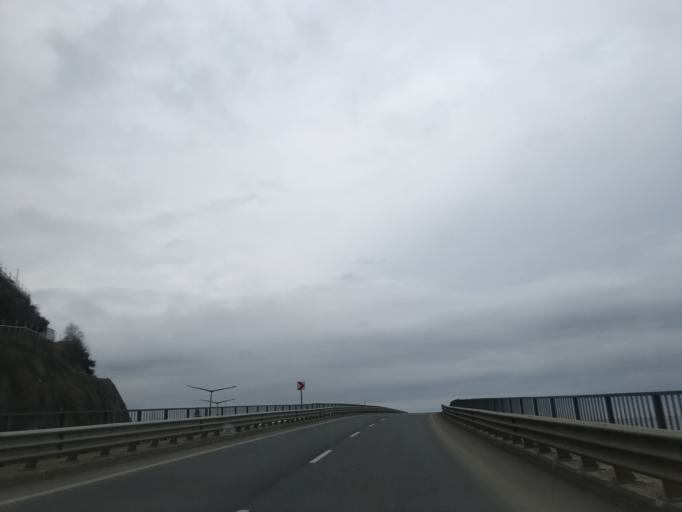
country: TR
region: Trabzon
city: Akcaabat
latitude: 41.0011
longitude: 39.6369
